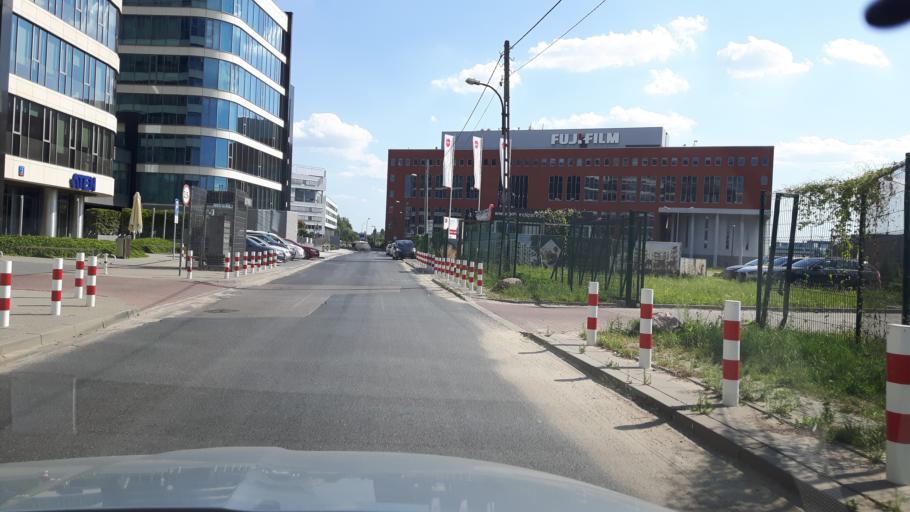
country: PL
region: Masovian Voivodeship
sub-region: Warszawa
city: Wlochy
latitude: 52.2054
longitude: 20.9384
